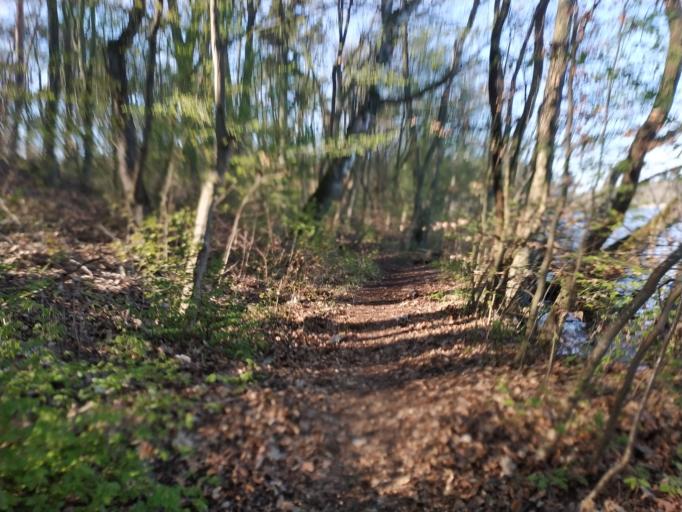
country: DE
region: Brandenburg
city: Strausberg
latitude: 52.5704
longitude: 13.8259
